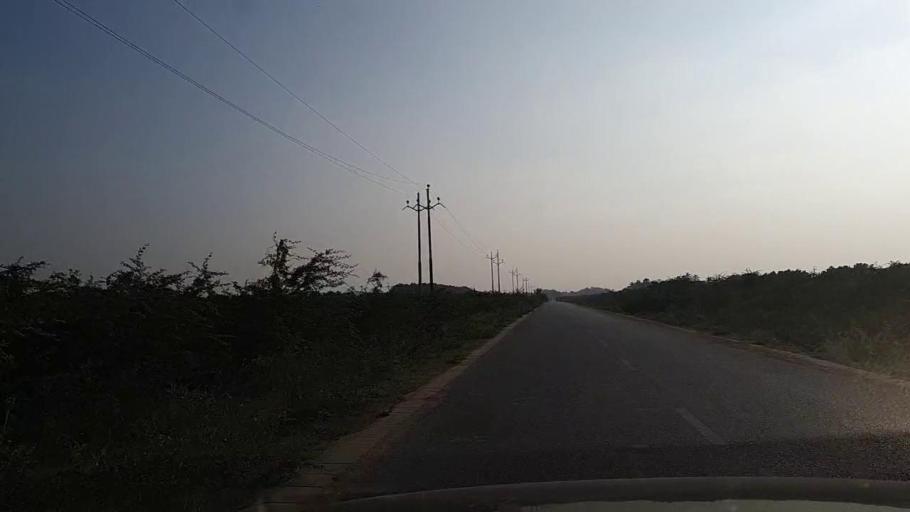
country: PK
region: Sindh
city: Gharo
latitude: 24.7890
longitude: 67.5151
